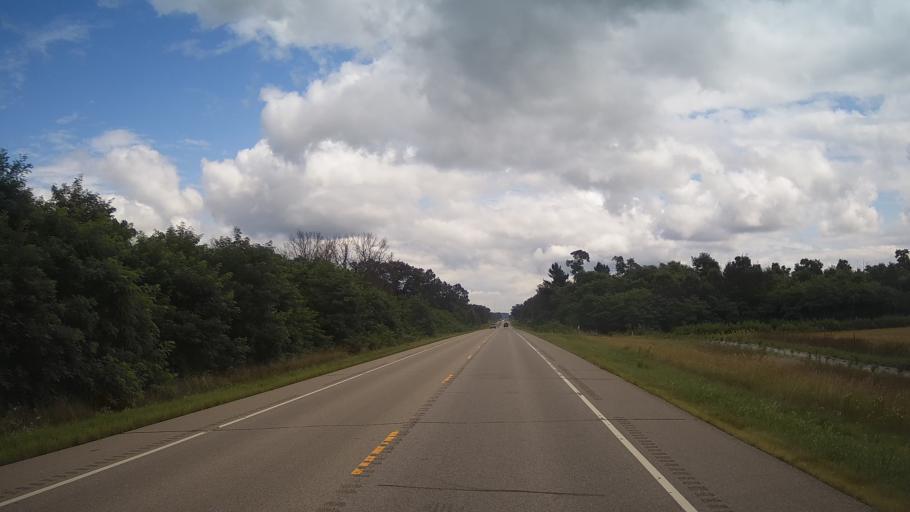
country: US
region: Wisconsin
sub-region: Adams County
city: Friendship
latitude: 44.0220
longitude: -89.6501
